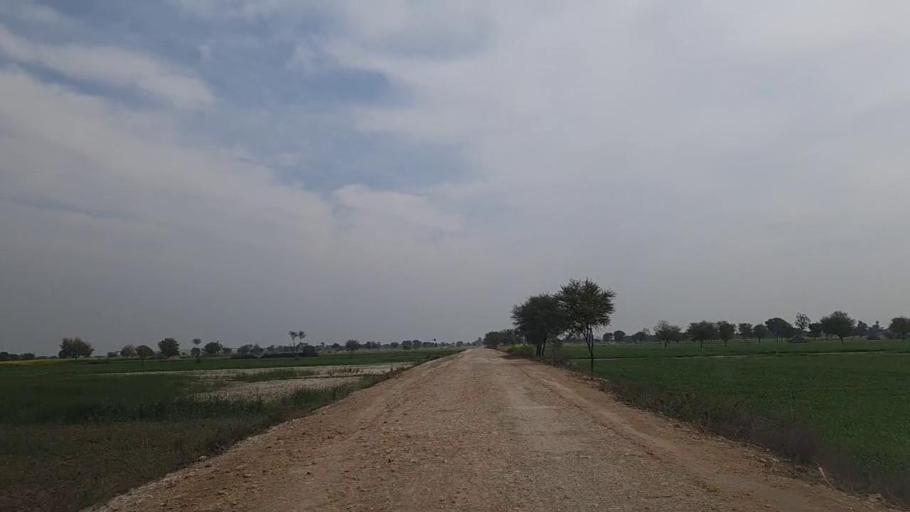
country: PK
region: Sindh
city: Daur
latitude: 26.4450
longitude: 68.4662
